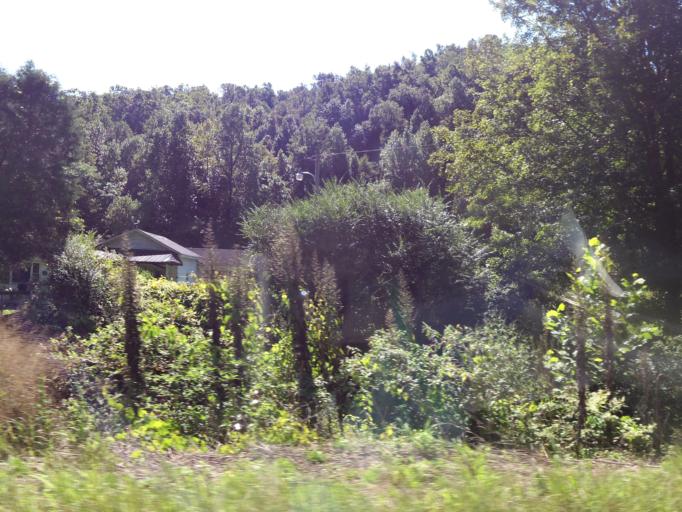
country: US
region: Kentucky
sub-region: Clay County
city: Manchester
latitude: 37.1280
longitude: -83.6247
